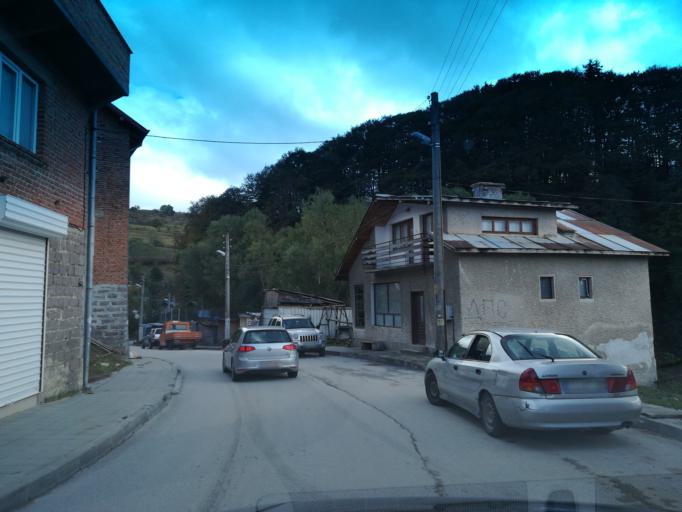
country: BG
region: Pazardzhik
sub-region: Obshtina Batak
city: Batak
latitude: 41.9366
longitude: 24.2708
